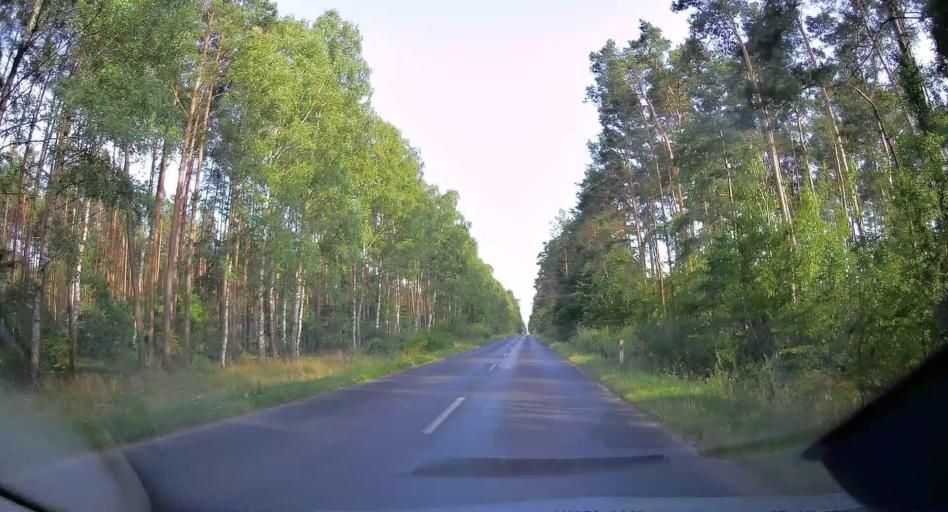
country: PL
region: Swietokrzyskie
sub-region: Powiat konecki
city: Smykow
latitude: 51.1079
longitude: 20.3504
